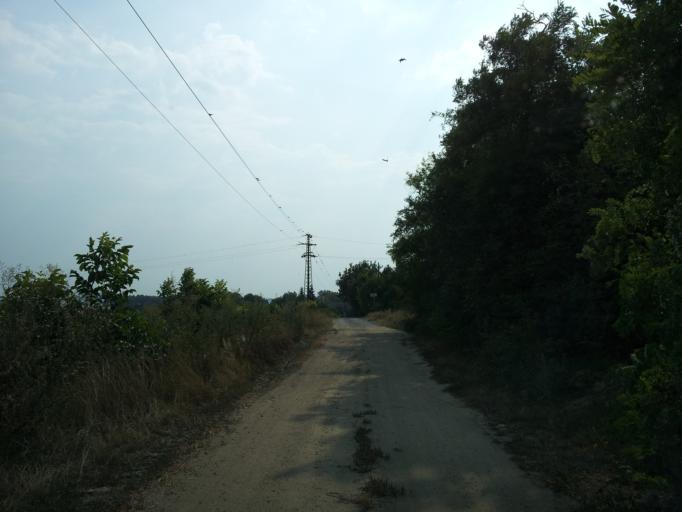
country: HU
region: Gyor-Moson-Sopron
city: Gyor
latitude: 47.6508
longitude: 17.6735
